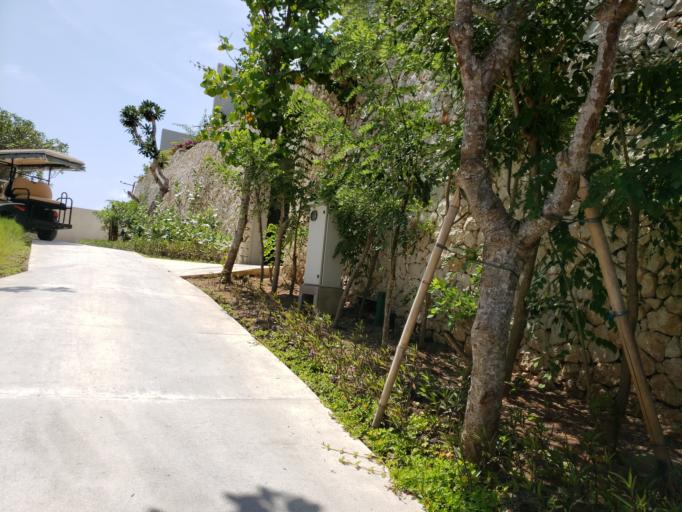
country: ID
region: Bali
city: Kangin
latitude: -8.8457
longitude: 115.1296
